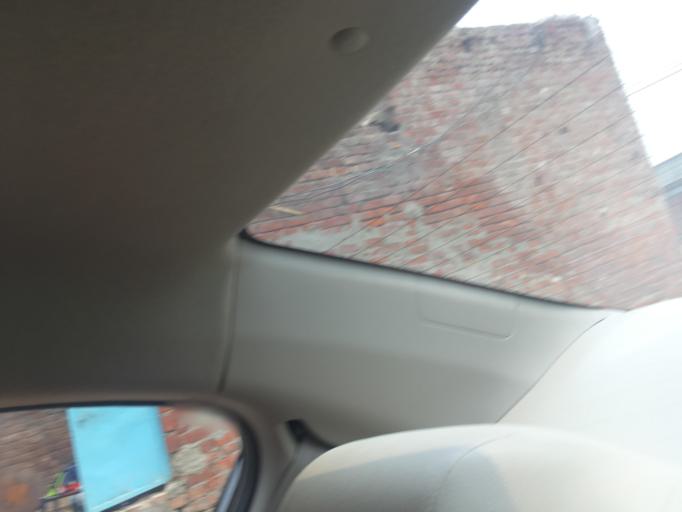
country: PK
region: Punjab
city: Lahore
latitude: 31.6142
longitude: 74.3544
